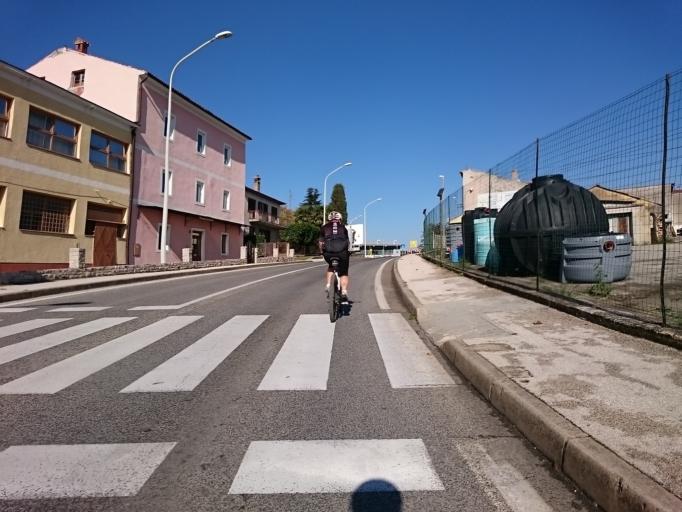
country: HR
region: Istarska
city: Buje
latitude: 45.4134
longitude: 13.6629
